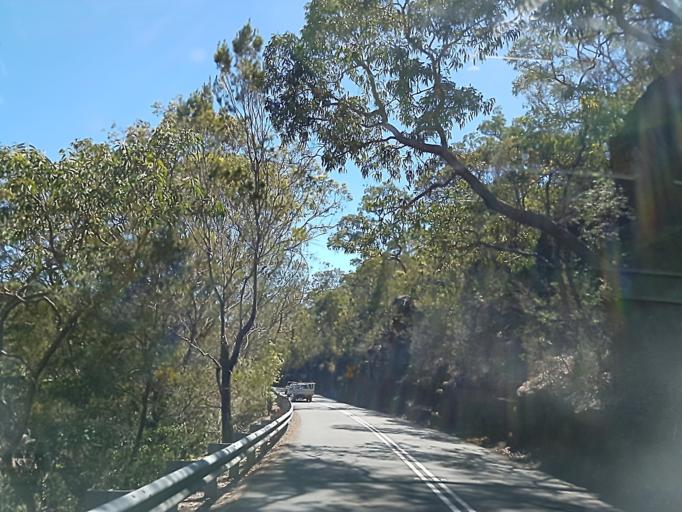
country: AU
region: New South Wales
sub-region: Hornsby Shire
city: Hornsby Heights
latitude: -33.6631
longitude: 151.0824
